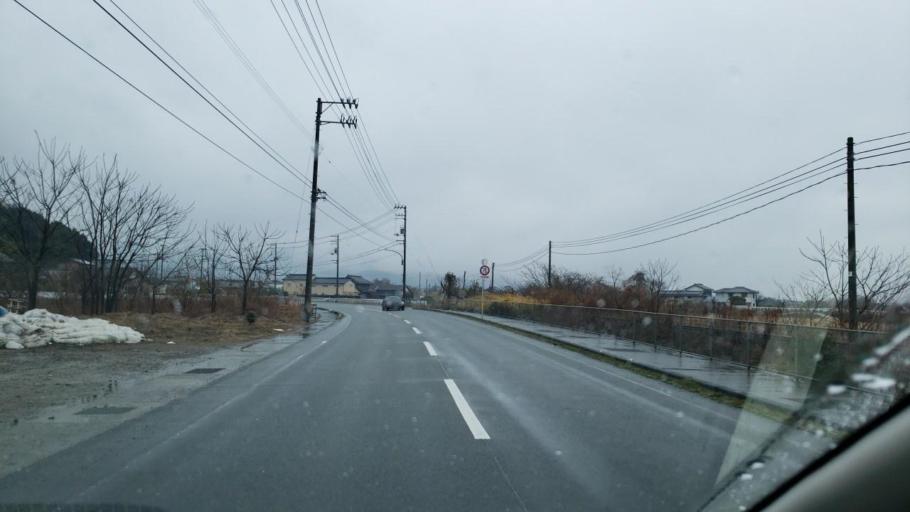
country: JP
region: Tokushima
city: Ishii
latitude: 34.1515
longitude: 134.4889
